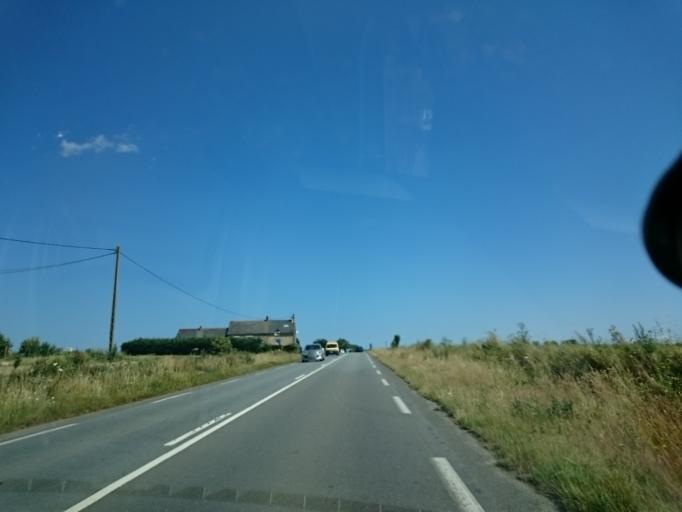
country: FR
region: Brittany
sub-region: Departement d'Ille-et-Vilaine
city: Saint-Meloir-des-Ondes
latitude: 48.6223
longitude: -1.9049
